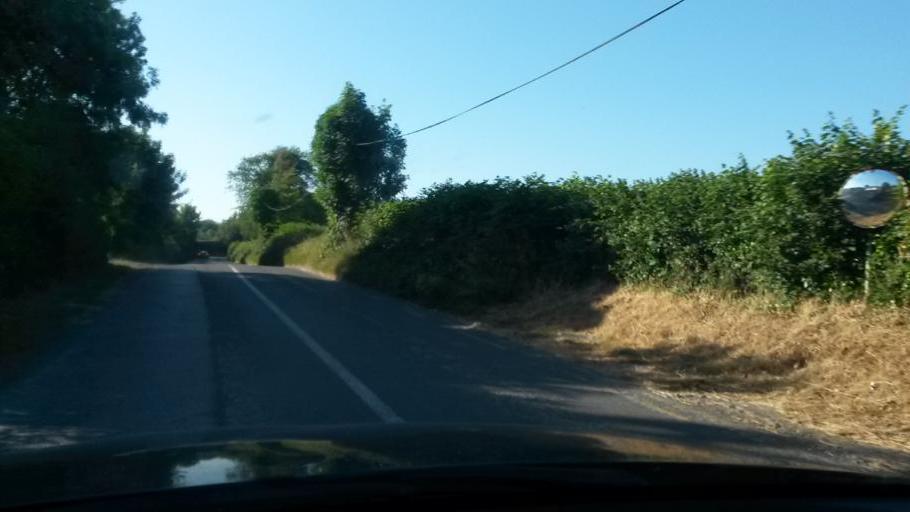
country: IE
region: Leinster
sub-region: Dublin City
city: Finglas
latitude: 53.4565
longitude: -6.3100
